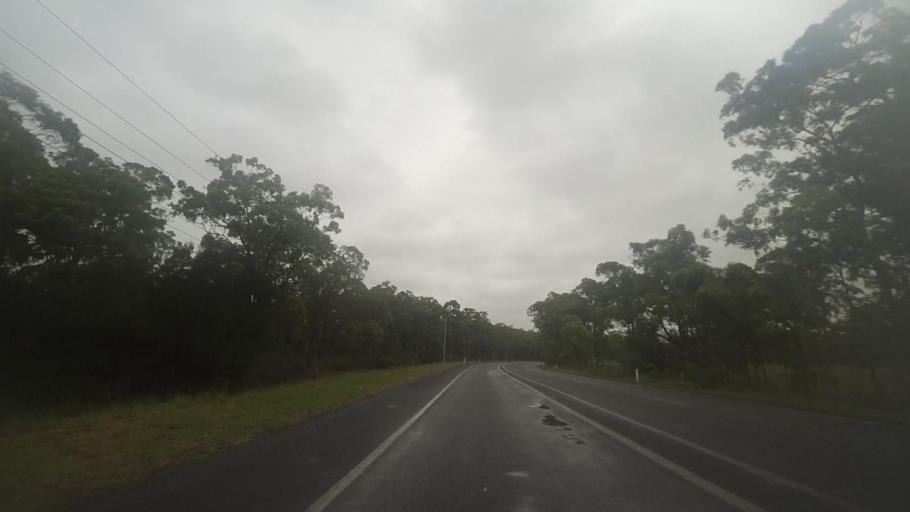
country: AU
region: New South Wales
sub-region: Port Stephens Shire
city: Port Stephens
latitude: -32.6469
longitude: 151.9805
